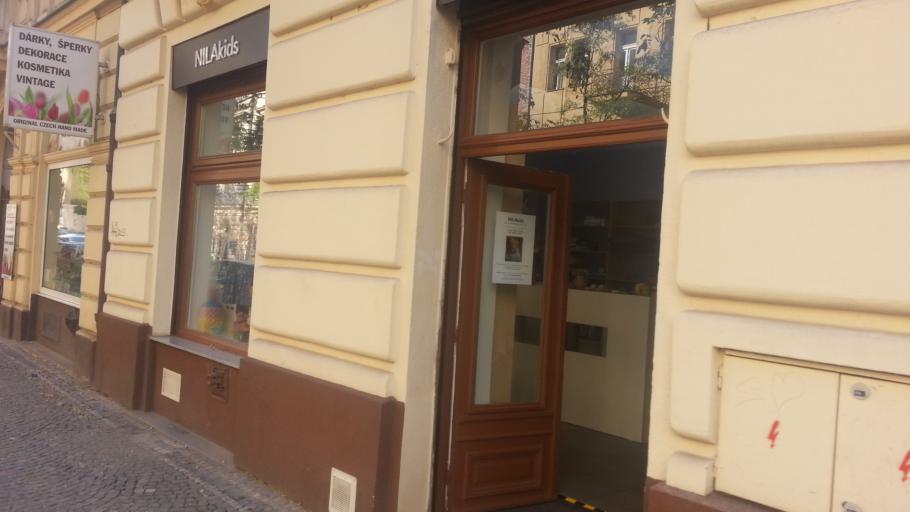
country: CZ
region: Praha
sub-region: Praha 8
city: Karlin
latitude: 50.0755
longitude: 14.4515
